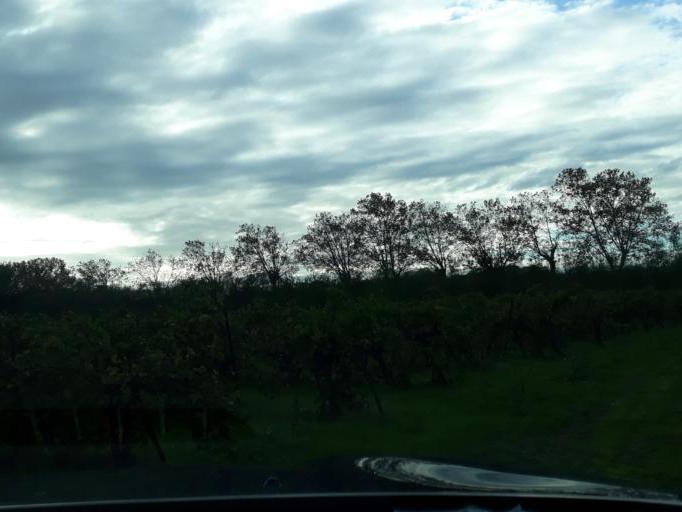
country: FR
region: Languedoc-Roussillon
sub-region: Departement de l'Herault
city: Bessan
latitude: 43.3661
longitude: 3.4303
